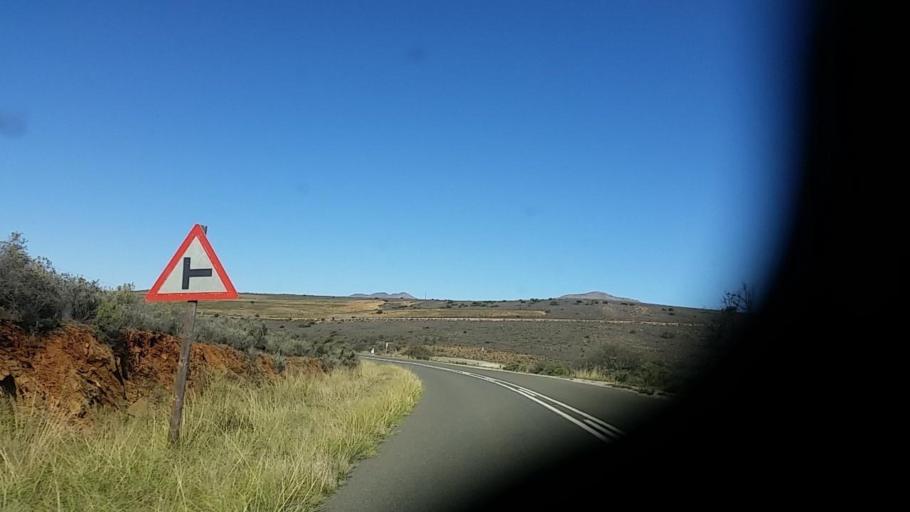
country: ZA
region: Western Cape
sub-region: Eden District Municipality
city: Knysna
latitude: -33.6277
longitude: 23.1220
